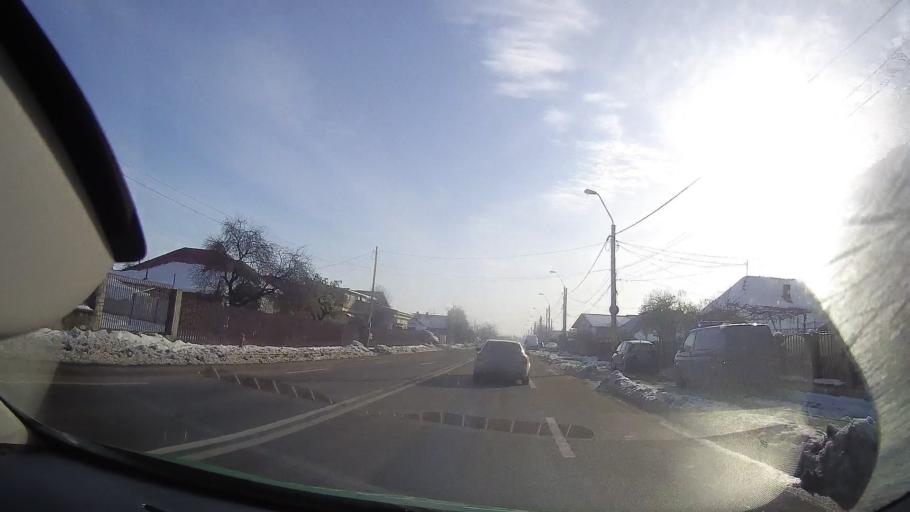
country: RO
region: Neamt
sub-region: Comuna Garcina
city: Garcina
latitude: 46.9594
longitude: 26.3823
